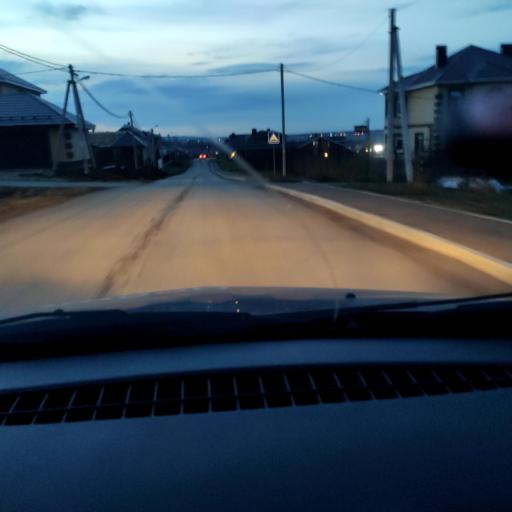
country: RU
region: Bashkortostan
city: Mikhaylovka
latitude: 54.8310
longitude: 55.8741
